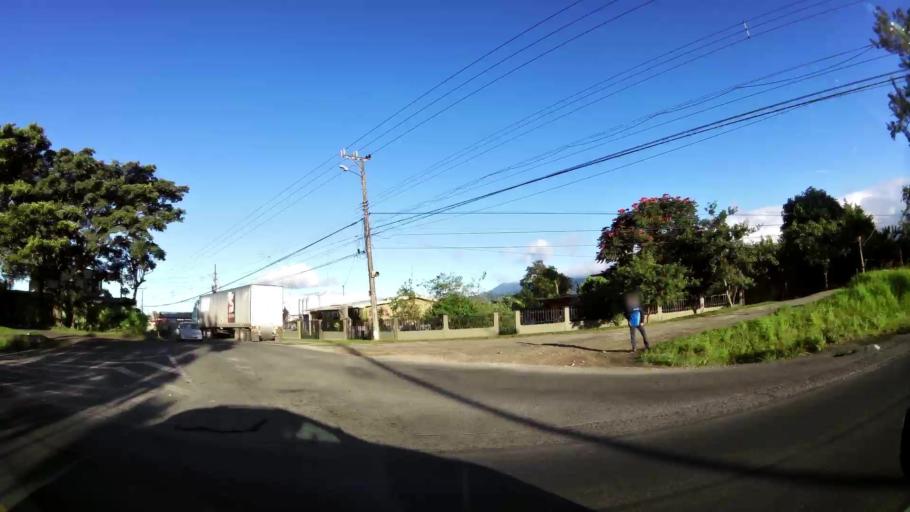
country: CR
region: Heredia
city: Angeles
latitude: 9.9910
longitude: -84.0403
